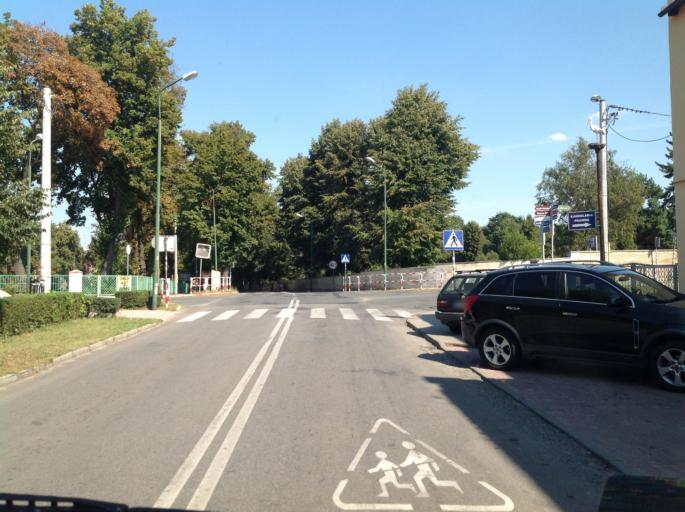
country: PL
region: Lower Silesian Voivodeship
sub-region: Powiat zabkowicki
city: Ziebice
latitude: 50.5988
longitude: 17.0440
